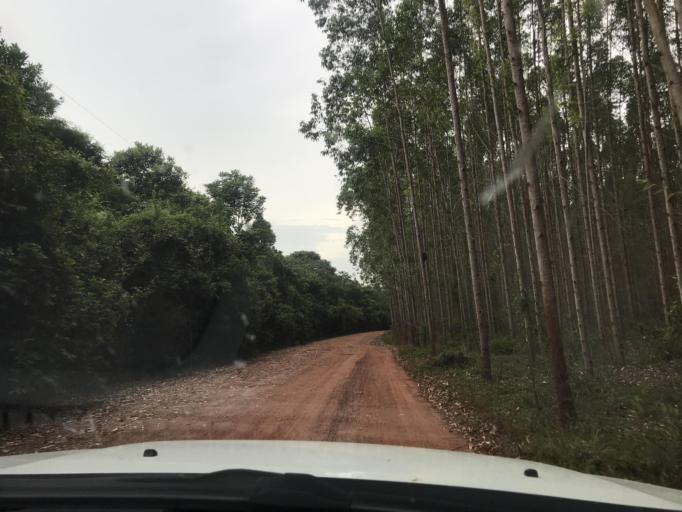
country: BR
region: Bahia
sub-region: Entre Rios
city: Entre Rios
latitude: -12.1060
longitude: -38.1869
